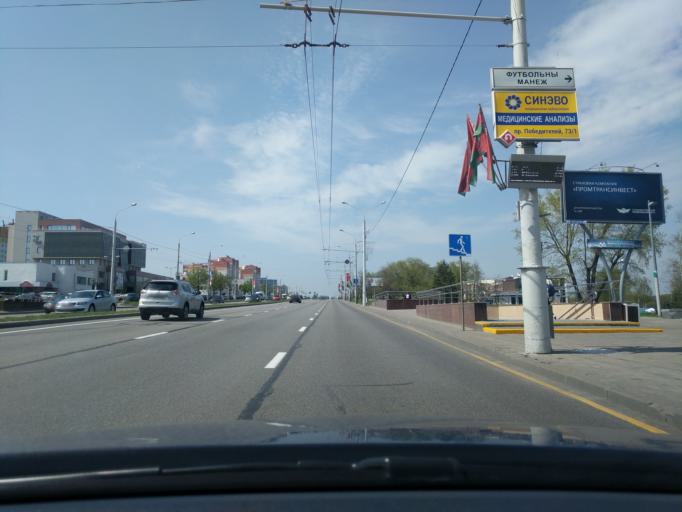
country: BY
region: Minsk
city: Minsk
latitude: 53.9324
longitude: 27.5073
